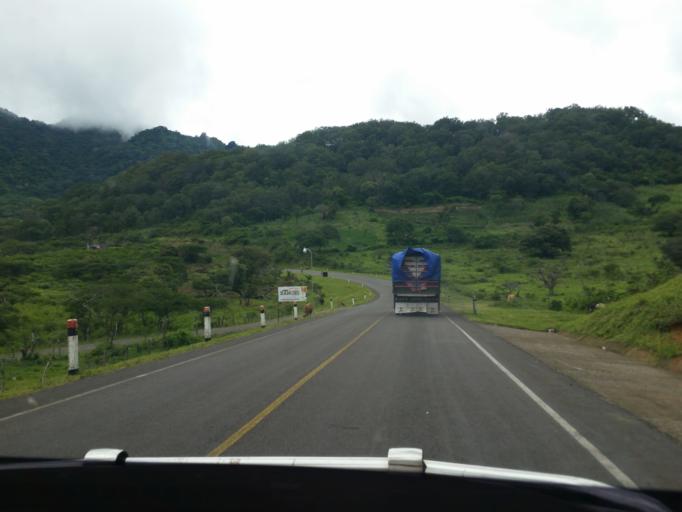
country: NI
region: Jinotega
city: Jinotega
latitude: 13.0622
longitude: -85.9958
